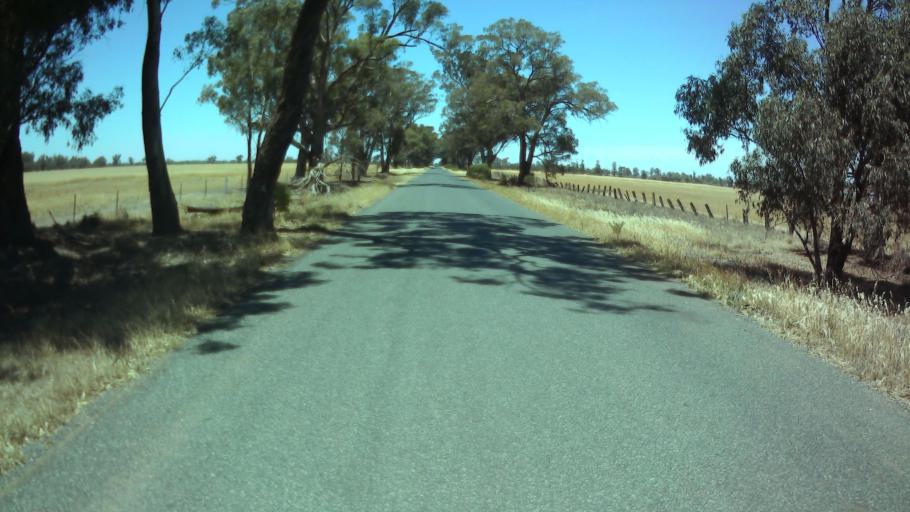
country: AU
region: New South Wales
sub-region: Weddin
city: Grenfell
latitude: -34.0189
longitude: 147.7930
